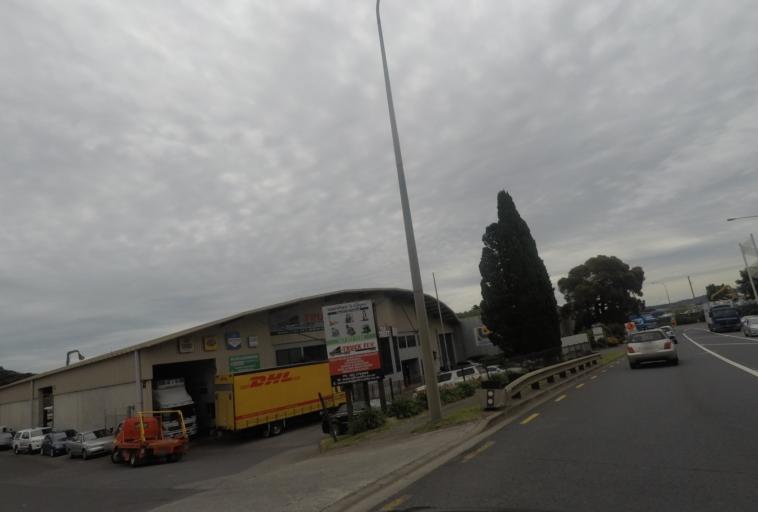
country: NZ
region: Auckland
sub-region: Auckland
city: Mangere
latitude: -36.9494
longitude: 174.8304
